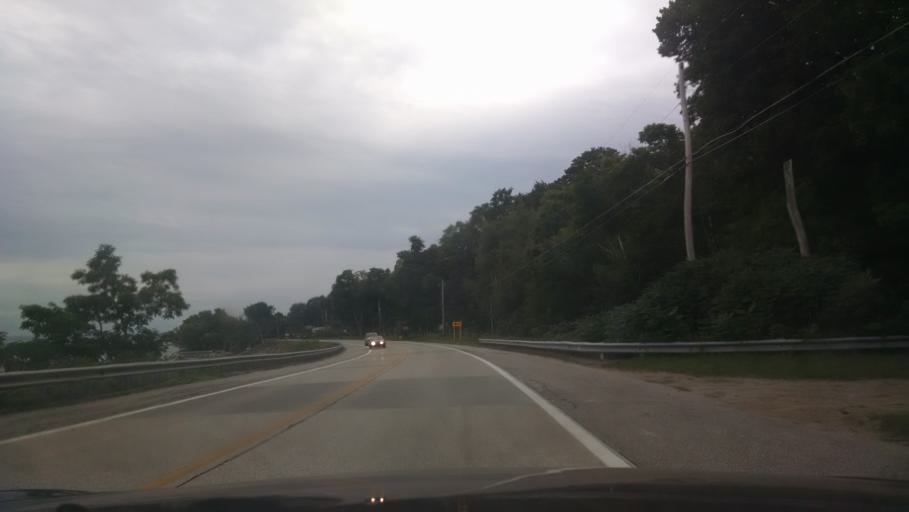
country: US
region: Michigan
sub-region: Leelanau County
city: Greilickville
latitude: 44.8661
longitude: -85.6492
